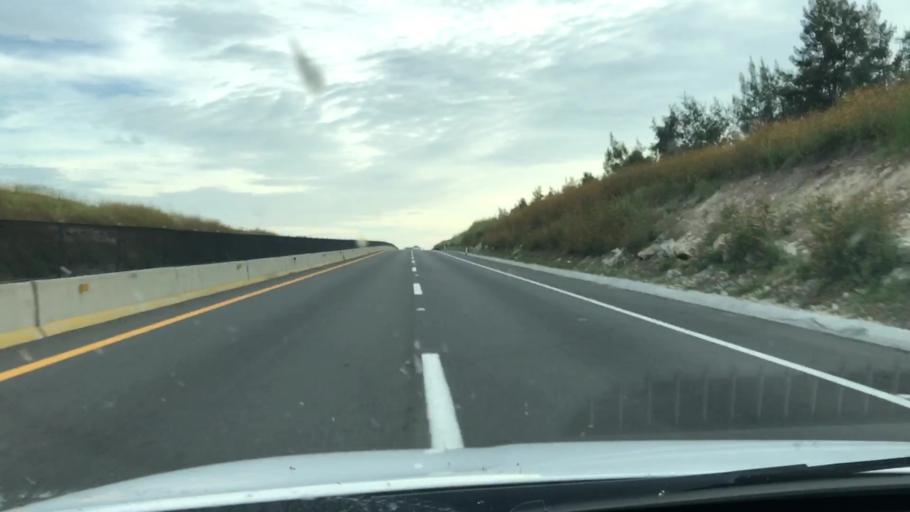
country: MX
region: Jalisco
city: San Juan de los Lagos
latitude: 21.2768
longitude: -102.2785
